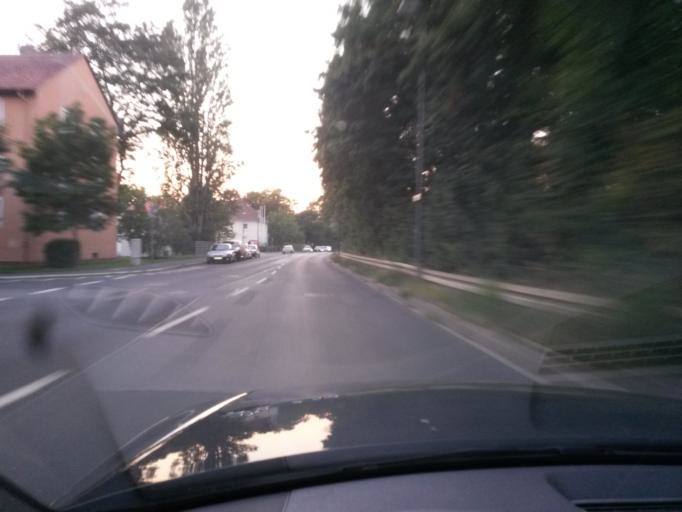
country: DE
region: Bavaria
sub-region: Regierungsbezirk Unterfranken
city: Randersacker
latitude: 49.7639
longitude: 9.9566
